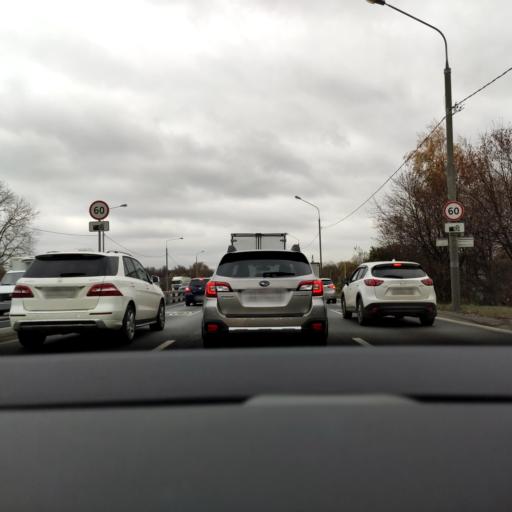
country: RU
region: Moskovskaya
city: Novopodrezkovo
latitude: 55.9314
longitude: 37.3782
